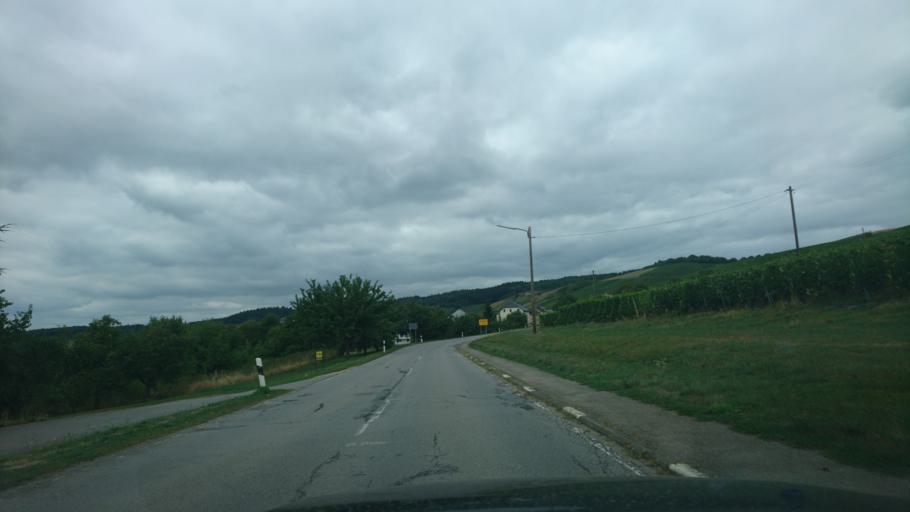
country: DE
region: Rheinland-Pfalz
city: Pellingen
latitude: 49.6844
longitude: 6.6405
